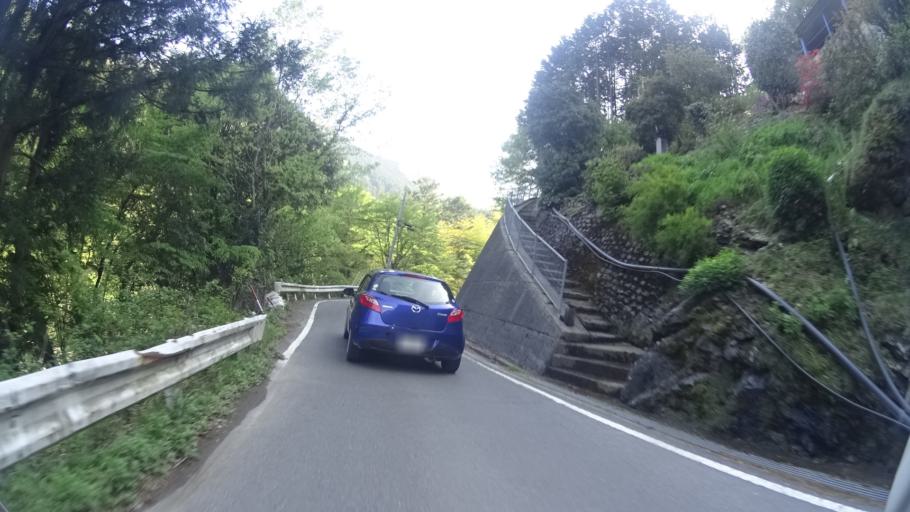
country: JP
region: Tokushima
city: Ikedacho
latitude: 33.8741
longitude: 133.9869
